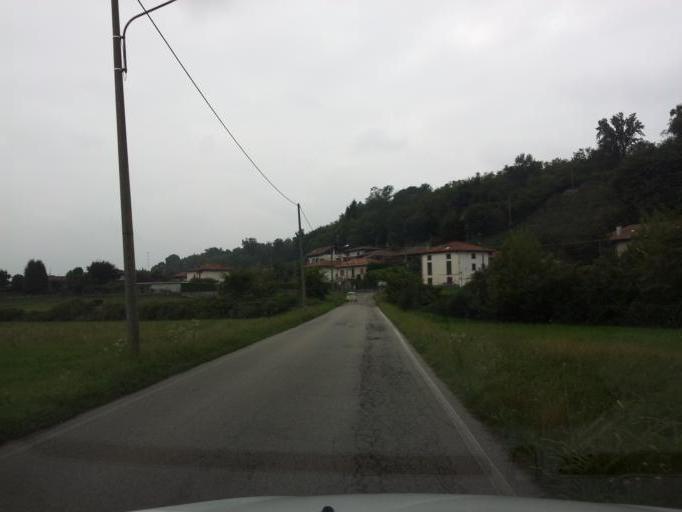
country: IT
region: Lombardy
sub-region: Provincia di Varese
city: Mercallo
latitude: 45.7358
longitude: 8.6648
